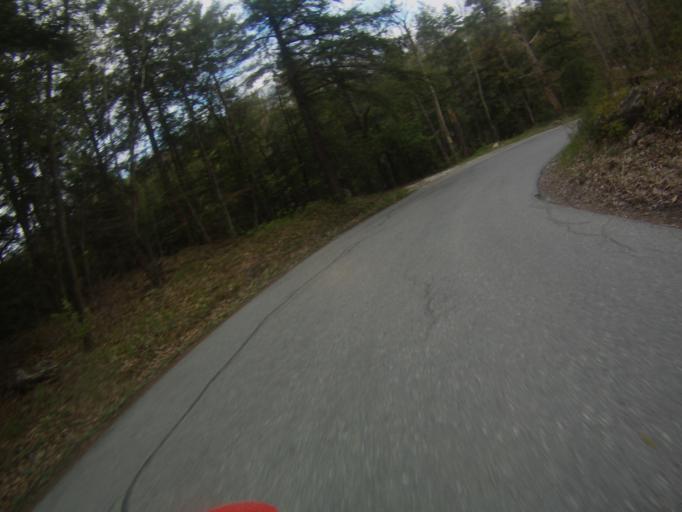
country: US
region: Vermont
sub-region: Addison County
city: Middlebury (village)
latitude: 43.9708
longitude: -73.0844
